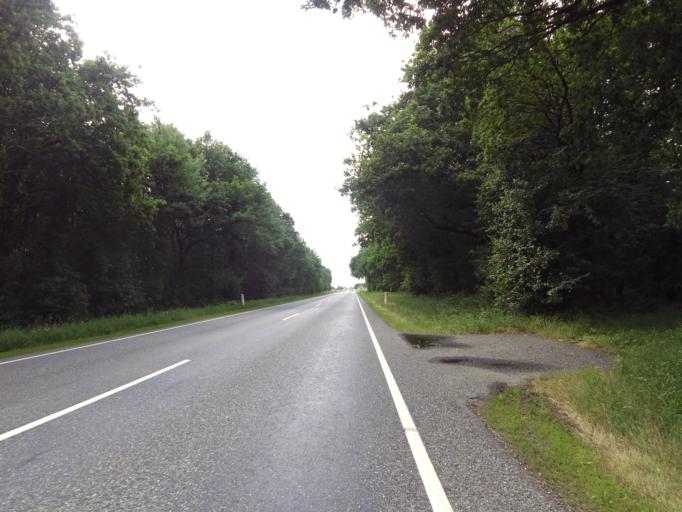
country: DK
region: South Denmark
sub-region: Haderslev Kommune
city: Gram
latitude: 55.2296
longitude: 8.9282
